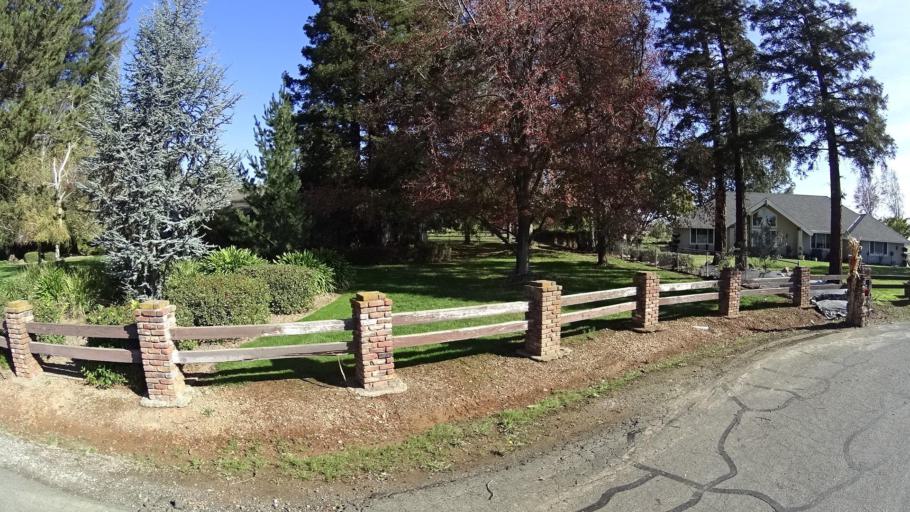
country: US
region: California
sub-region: Sacramento County
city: Elk Grove
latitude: 38.4352
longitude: -121.3610
